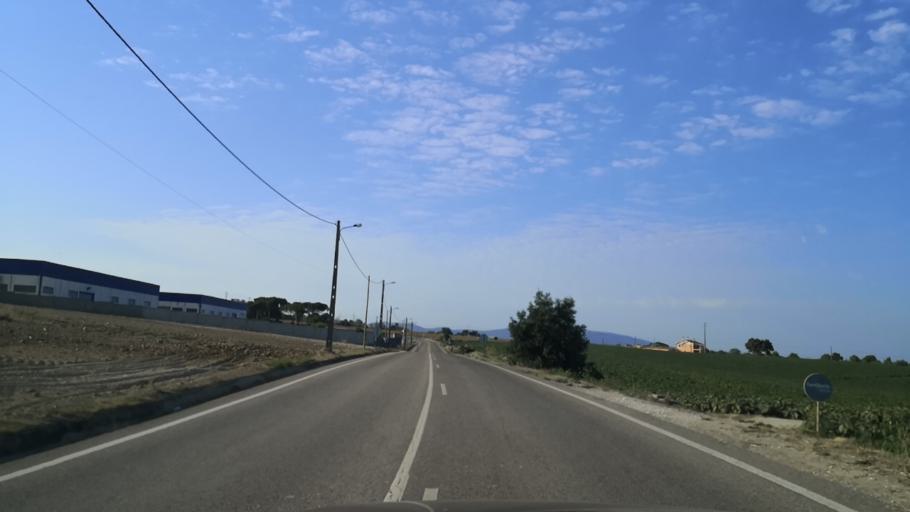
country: PT
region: Santarem
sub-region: Santarem
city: Santarem
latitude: 39.3425
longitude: -8.6609
